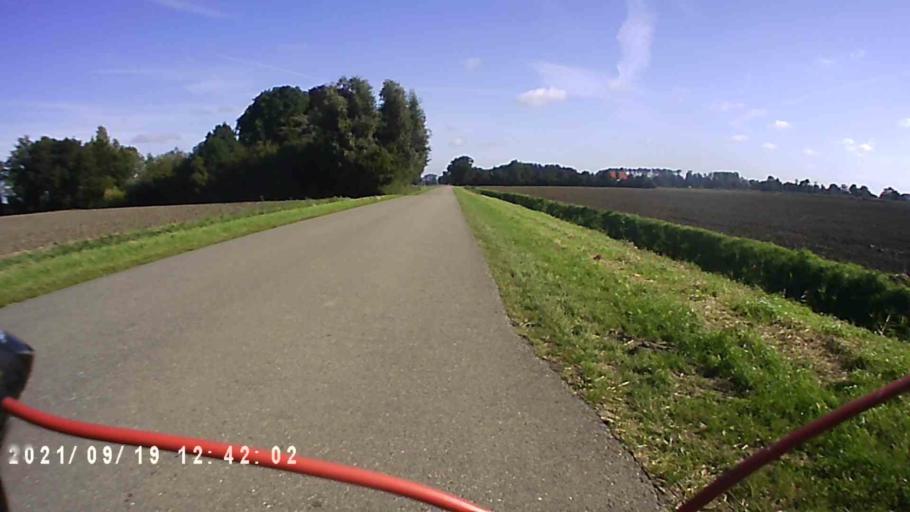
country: NL
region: Groningen
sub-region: Gemeente Delfzijl
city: Delfzijl
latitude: 53.2158
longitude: 6.9293
